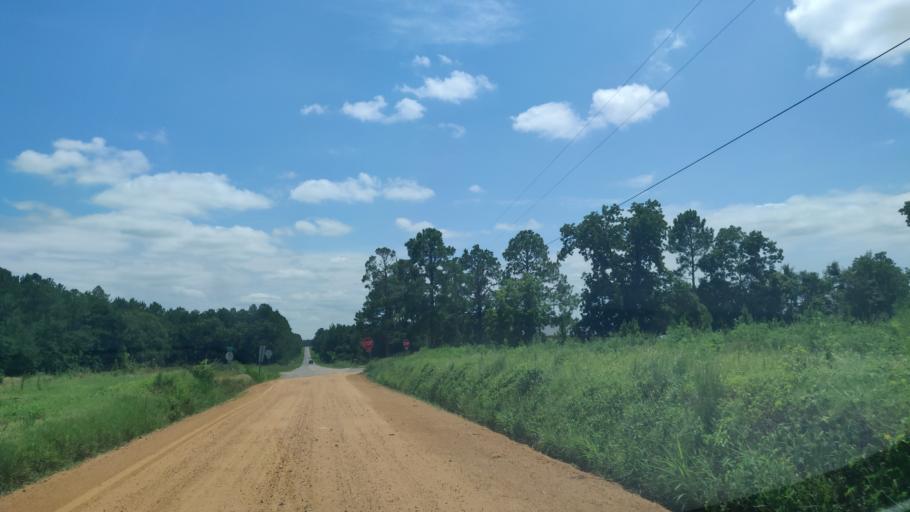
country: US
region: Georgia
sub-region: Tift County
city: Omega
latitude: 31.4611
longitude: -83.6374
